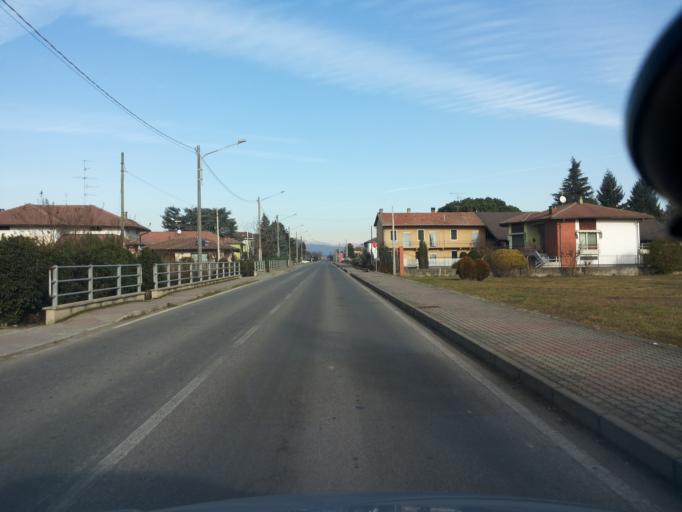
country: IT
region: Piedmont
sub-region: Provincia di Vercelli
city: Ghislarengo
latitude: 45.5322
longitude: 8.3858
